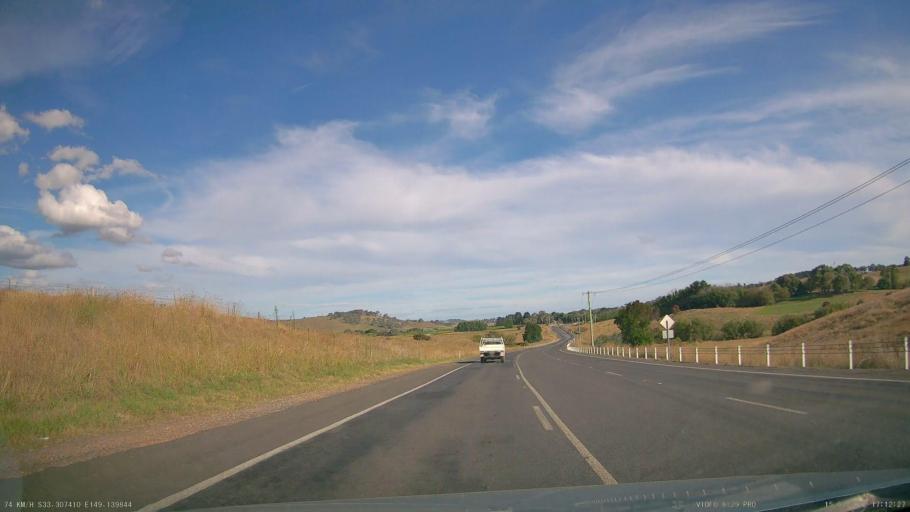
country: AU
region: New South Wales
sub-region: Orange Municipality
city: Orange
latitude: -33.3075
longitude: 149.1398
